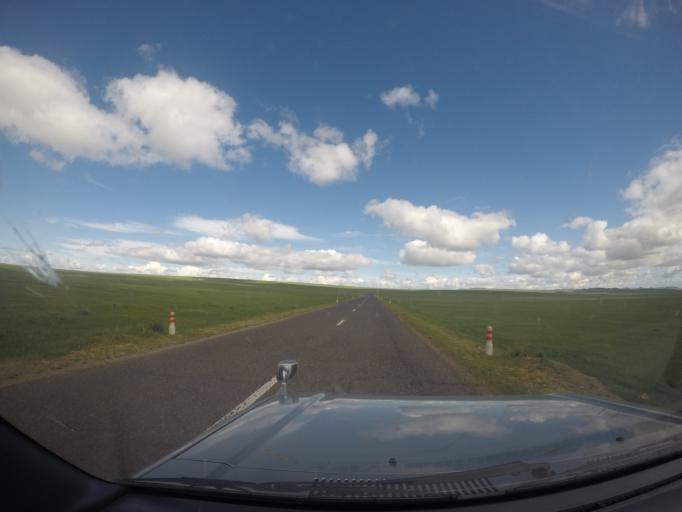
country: MN
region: Hentiy
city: Bayanbulag
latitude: 47.4626
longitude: 109.6202
